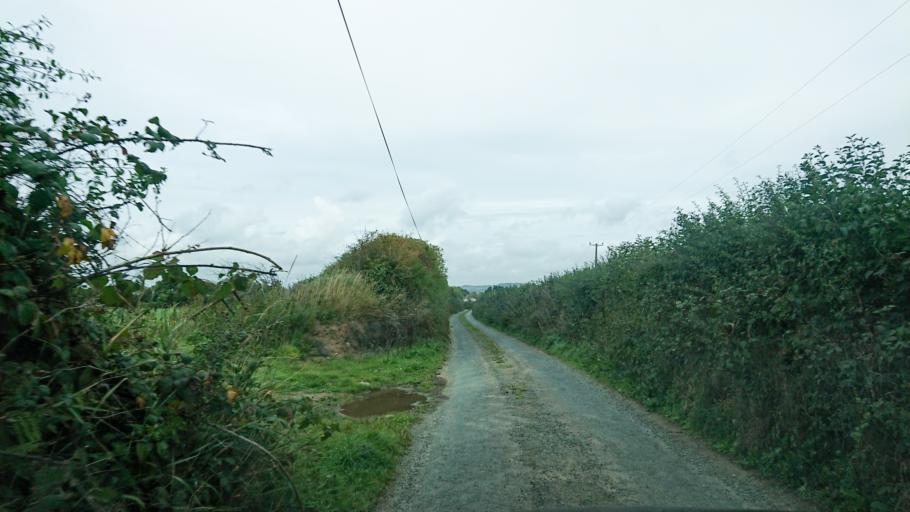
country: IE
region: Munster
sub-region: Waterford
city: Dunmore East
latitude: 52.2059
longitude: -7.0443
